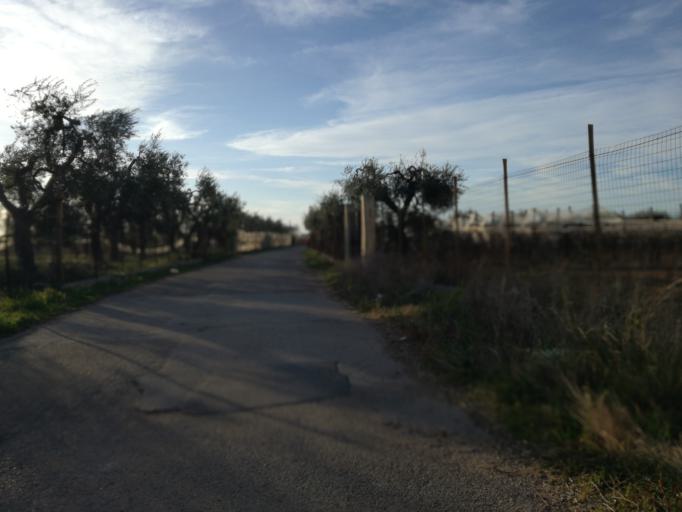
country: IT
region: Apulia
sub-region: Provincia di Bari
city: Valenzano
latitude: 41.0508
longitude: 16.9011
